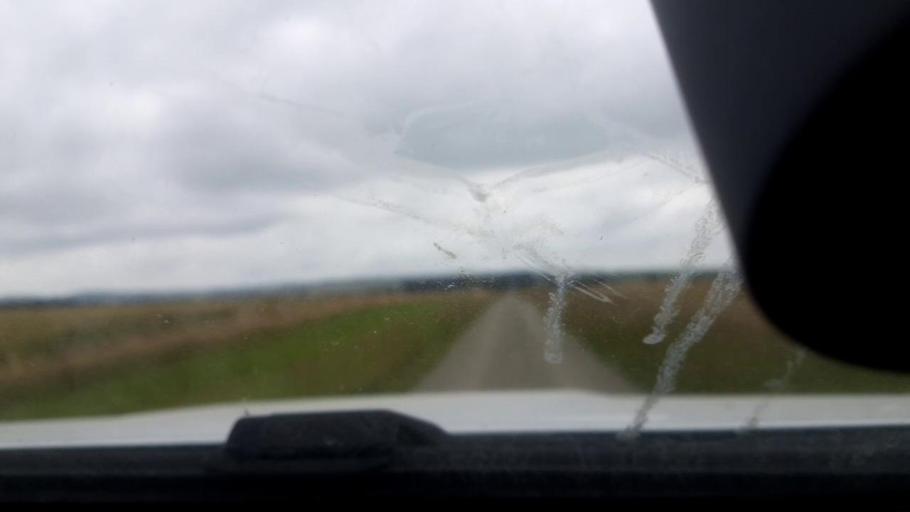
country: NZ
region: Canterbury
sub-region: Timaru District
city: Pleasant Point
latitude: -44.2301
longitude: 171.1662
